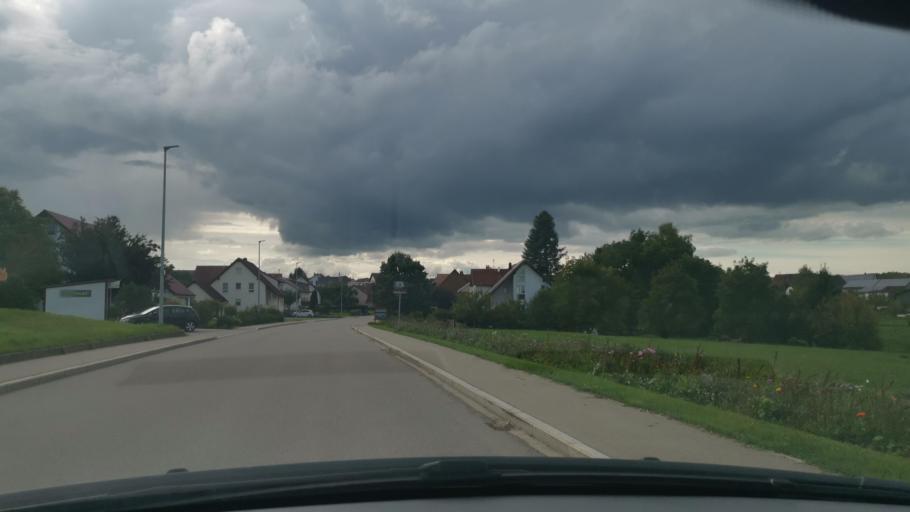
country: DE
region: Baden-Wuerttemberg
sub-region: Tuebingen Region
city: Lauterach
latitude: 48.3091
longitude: 9.6201
